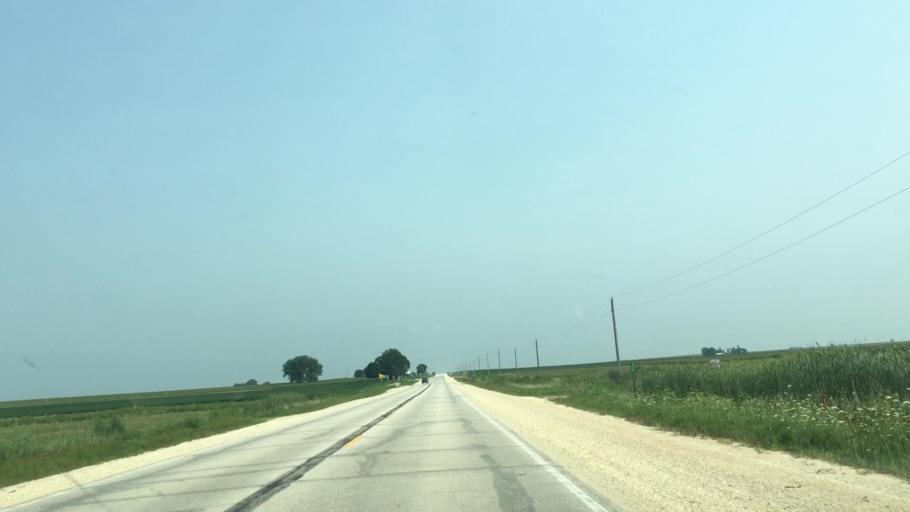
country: US
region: Iowa
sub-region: Fayette County
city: Oelwein
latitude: 42.6873
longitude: -91.8105
